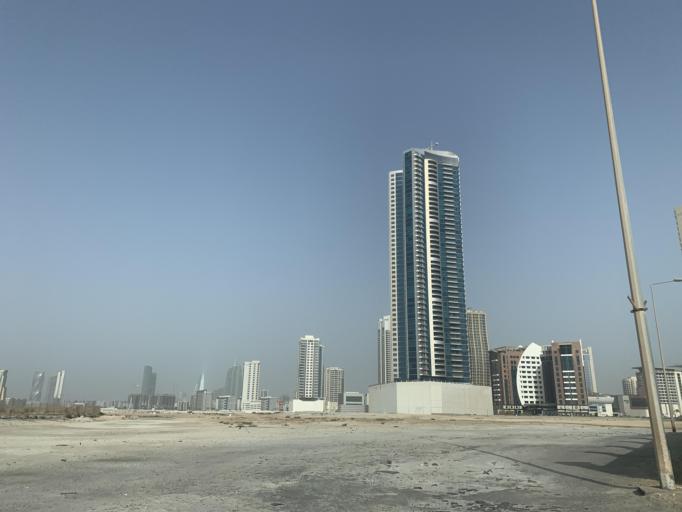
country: BH
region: Manama
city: Jidd Hafs
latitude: 26.2380
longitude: 50.5463
